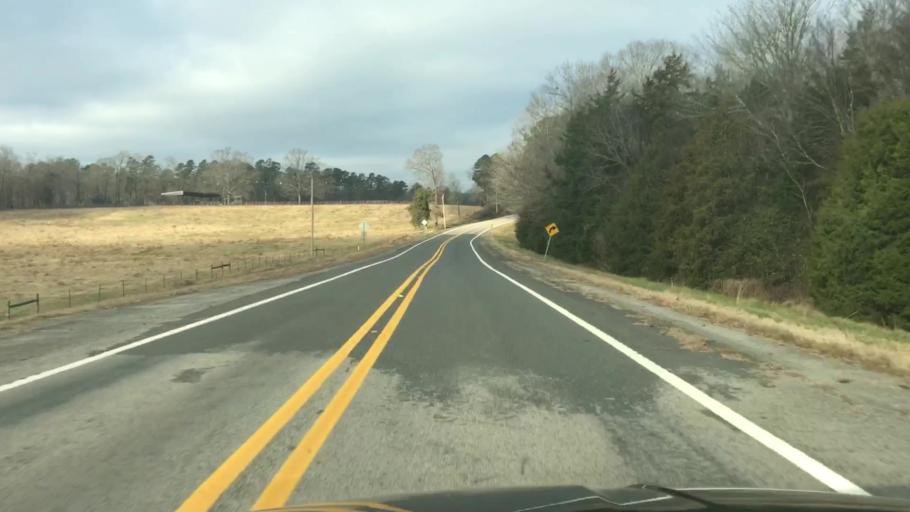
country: US
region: Arkansas
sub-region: Montgomery County
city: Mount Ida
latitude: 34.6595
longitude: -93.7645
